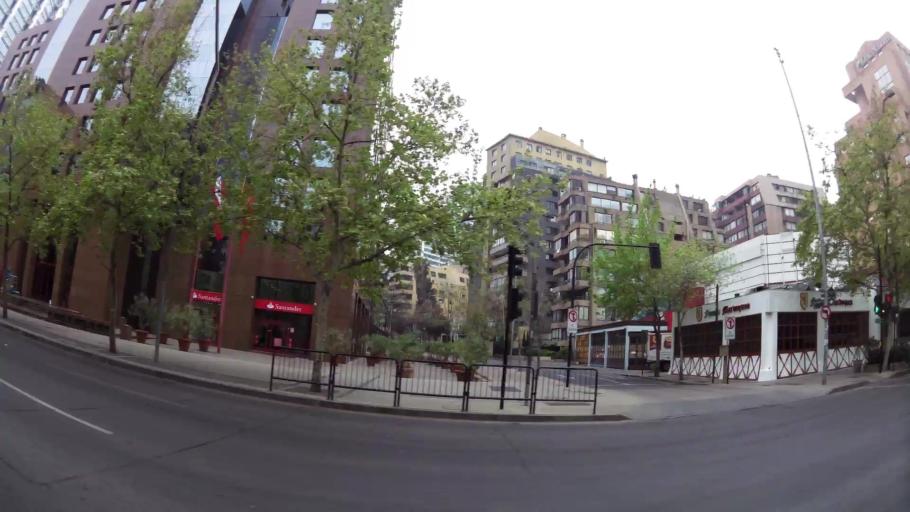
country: CL
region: Santiago Metropolitan
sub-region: Provincia de Santiago
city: Villa Presidente Frei, Nunoa, Santiago, Chile
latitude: -33.4153
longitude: -70.6010
